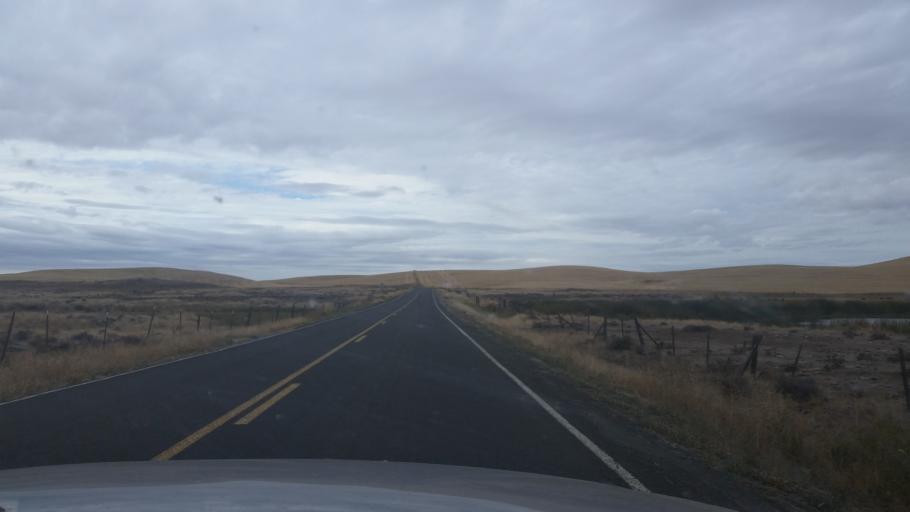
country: US
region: Washington
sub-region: Spokane County
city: Medical Lake
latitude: 47.5292
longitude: -117.8445
